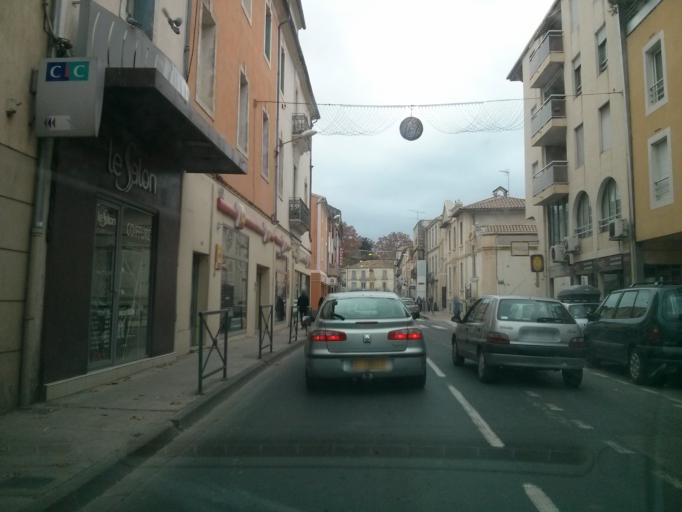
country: FR
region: Languedoc-Roussillon
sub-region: Departement de l'Herault
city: Lunel
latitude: 43.6767
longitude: 4.1333
